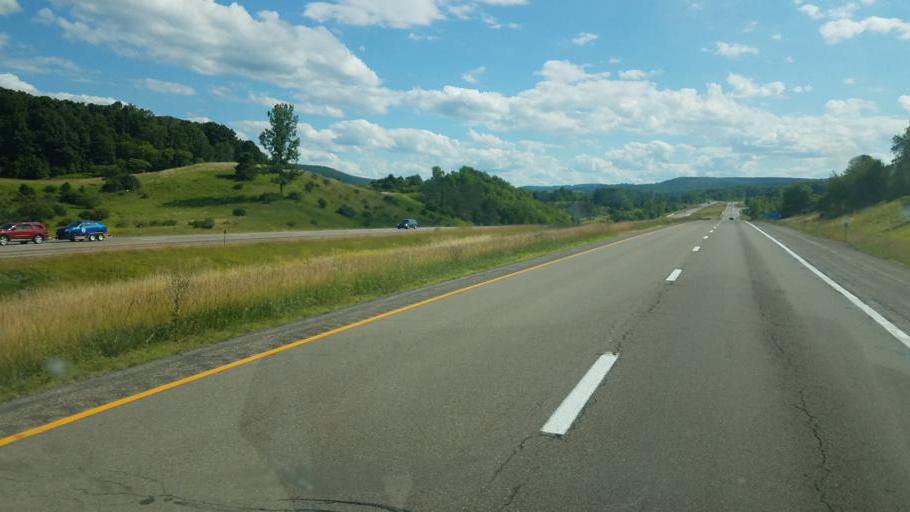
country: US
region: New York
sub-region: Steuben County
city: Hornell
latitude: 42.3305
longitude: -77.7366
